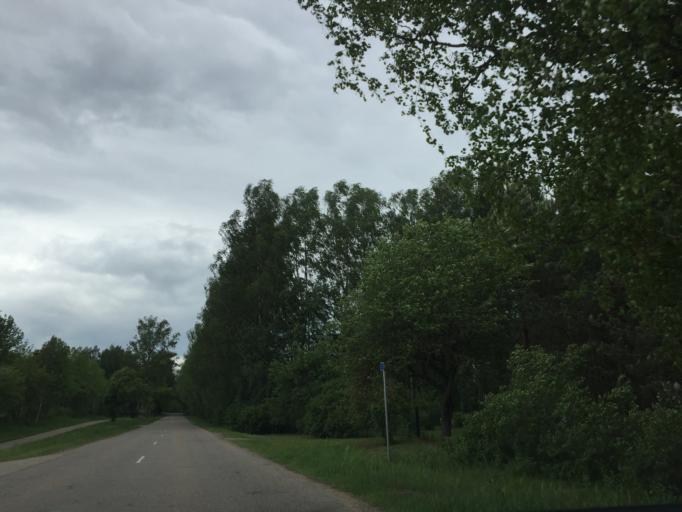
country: LV
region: Preilu Rajons
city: Preili
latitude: 56.0602
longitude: 26.7731
